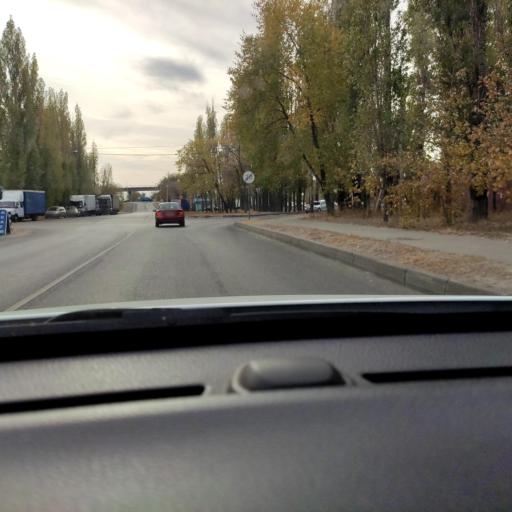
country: RU
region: Voronezj
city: Voronezh
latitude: 51.6914
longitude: 39.2528
